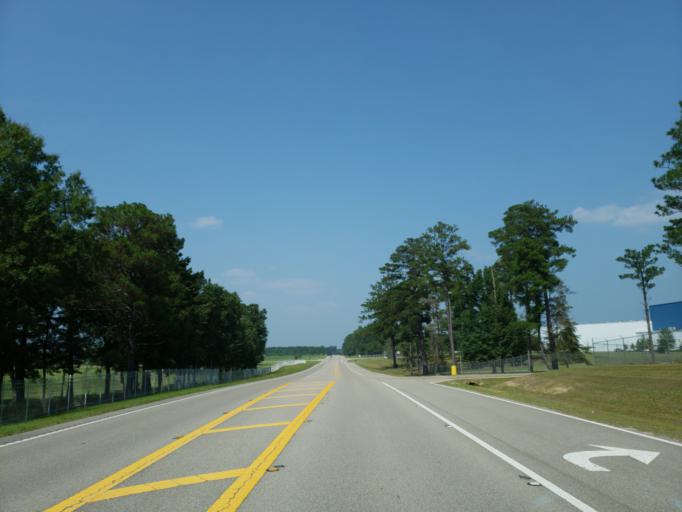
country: US
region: Mississippi
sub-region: Jones County
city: Ellisville
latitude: 31.5685
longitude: -89.2374
